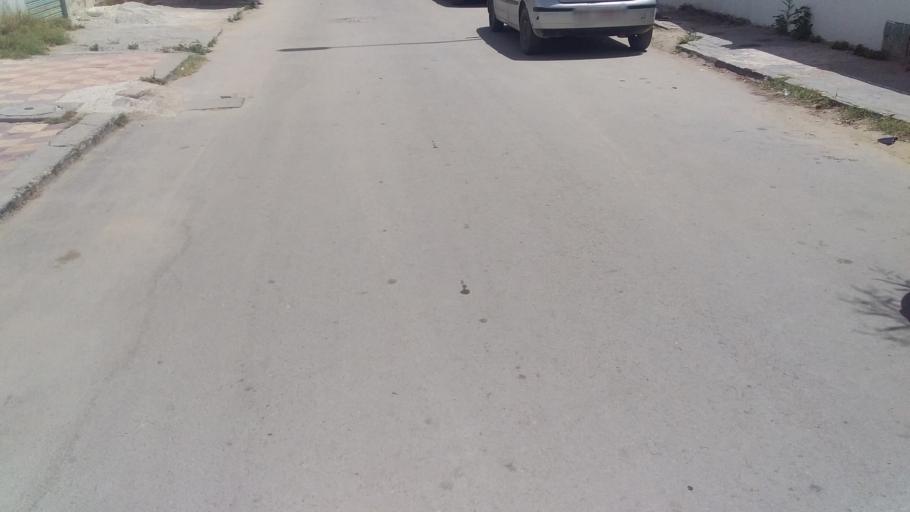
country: TN
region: Al Qayrawan
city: Kairouan
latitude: 35.6730
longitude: 10.1032
